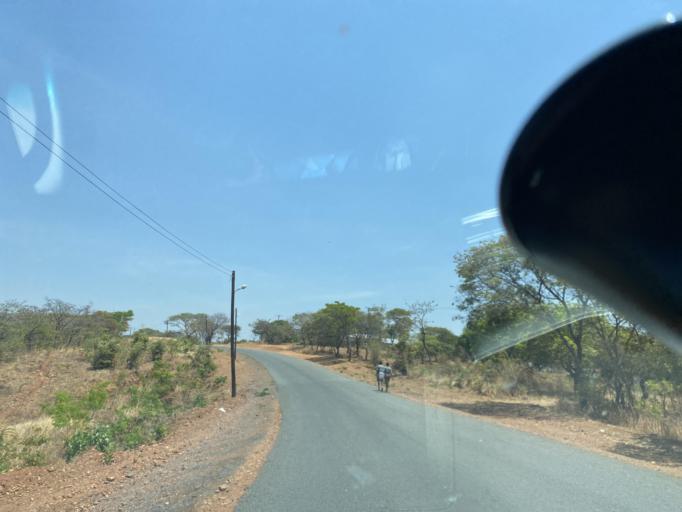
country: ZM
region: Lusaka
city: Kafue
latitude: -15.8655
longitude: 28.4429
